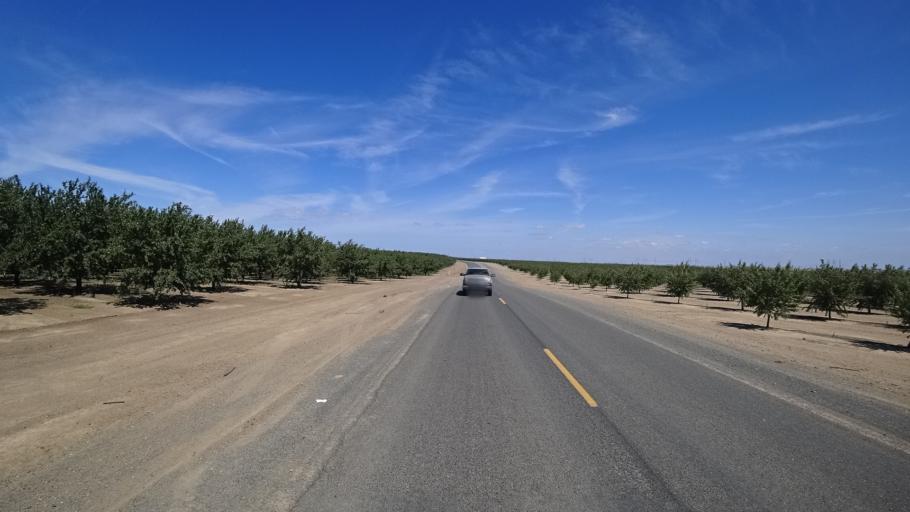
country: US
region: California
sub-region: Kings County
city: Kettleman City
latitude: 35.9496
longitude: -119.9315
